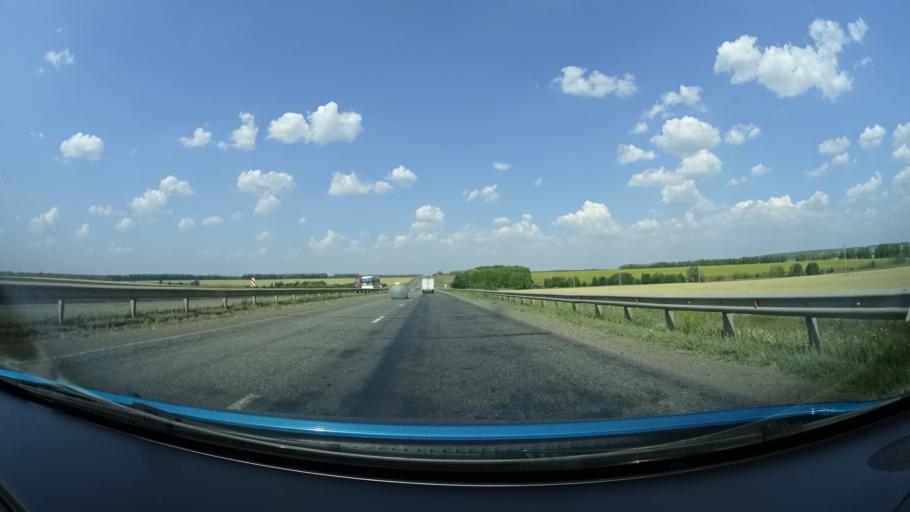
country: RU
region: Bashkortostan
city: Dmitriyevka
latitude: 54.6855
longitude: 55.3154
